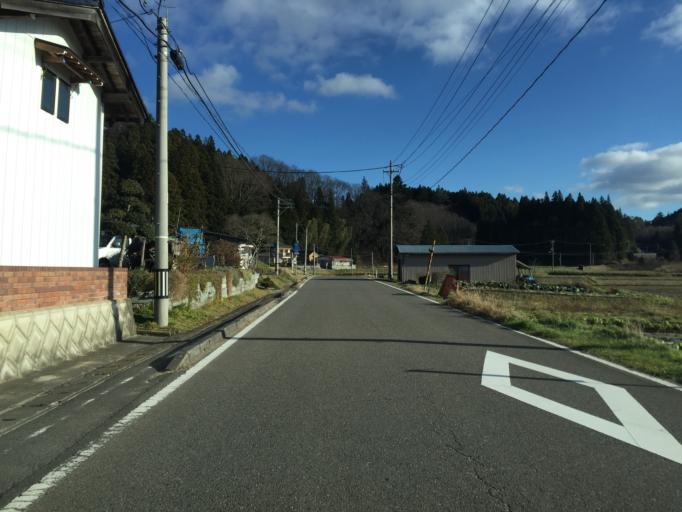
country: JP
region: Fukushima
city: Funehikimachi-funehiki
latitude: 37.2497
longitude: 140.6687
